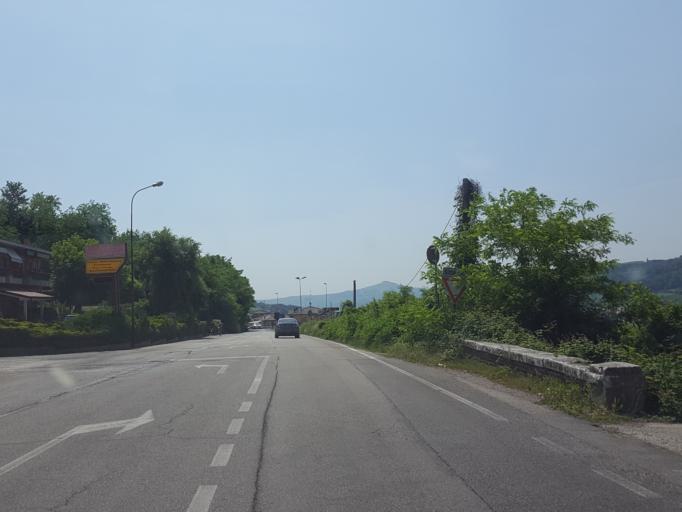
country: IT
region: Veneto
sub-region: Provincia di Verona
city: San Giovanni Ilarione
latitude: 45.5141
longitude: 11.2404
